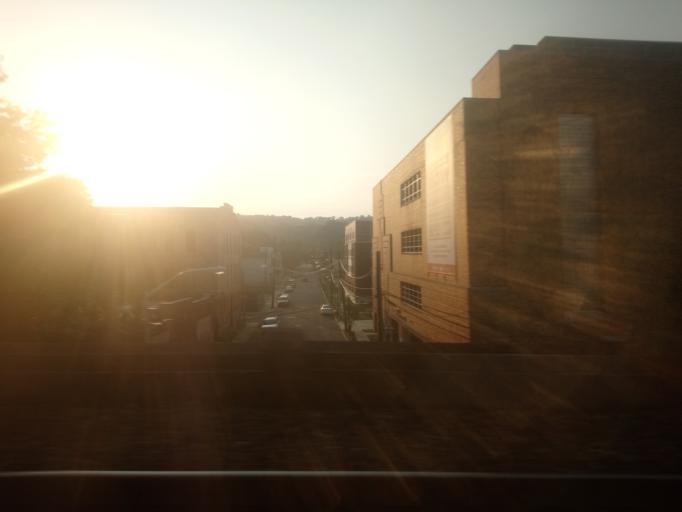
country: US
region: New Jersey
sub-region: Essex County
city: Orange
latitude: 40.7681
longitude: -74.2428
